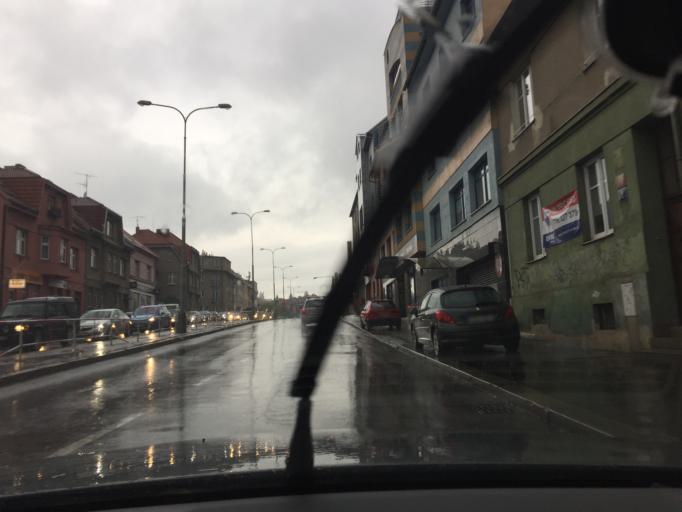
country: CZ
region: Praha
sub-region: Praha 8
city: Liben
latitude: 50.1220
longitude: 14.4549
